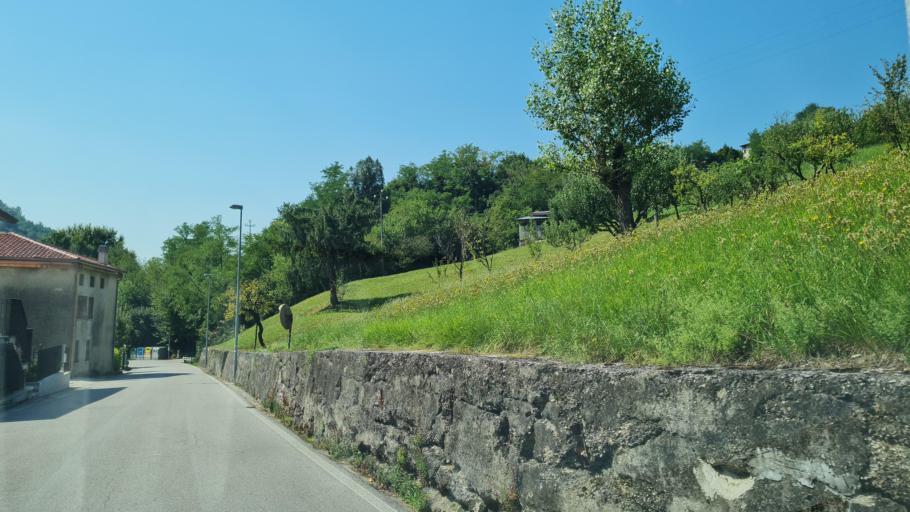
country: IT
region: Veneto
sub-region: Provincia di Vicenza
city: Salcedo
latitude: 45.7588
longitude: 11.5926
